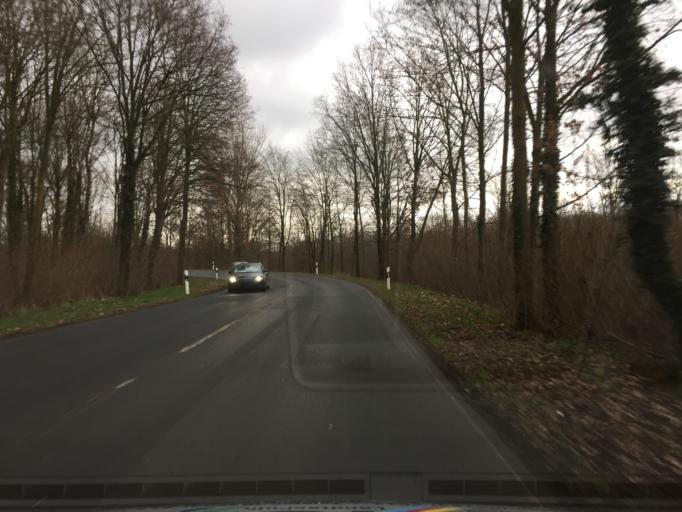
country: DE
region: Lower Saxony
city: Stolzenau
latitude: 52.5082
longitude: 9.0787
